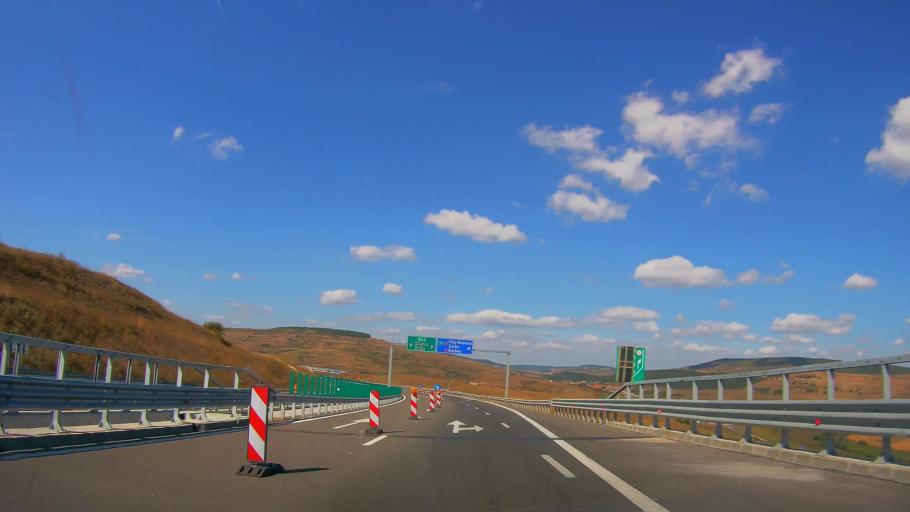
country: RO
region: Cluj
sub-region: Comuna Baciu
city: Mera
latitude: 46.8049
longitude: 23.4263
